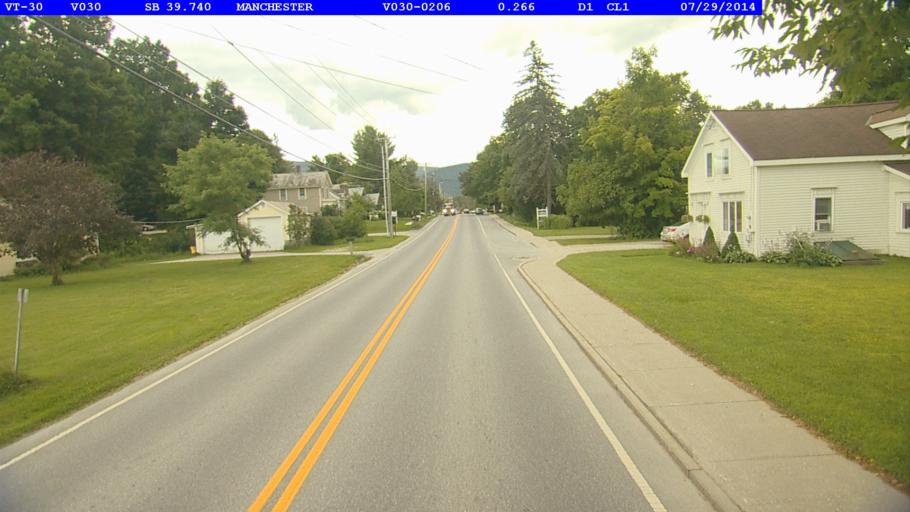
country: US
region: Vermont
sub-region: Bennington County
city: Manchester Center
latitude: 43.1806
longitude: -73.0577
